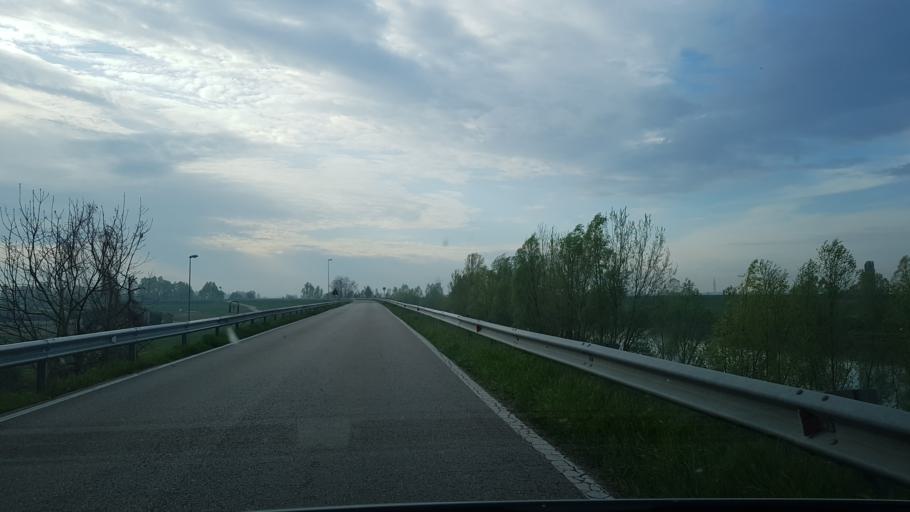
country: IT
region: Veneto
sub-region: Provincia di Rovigo
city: Lendinara
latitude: 45.1176
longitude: 11.6017
